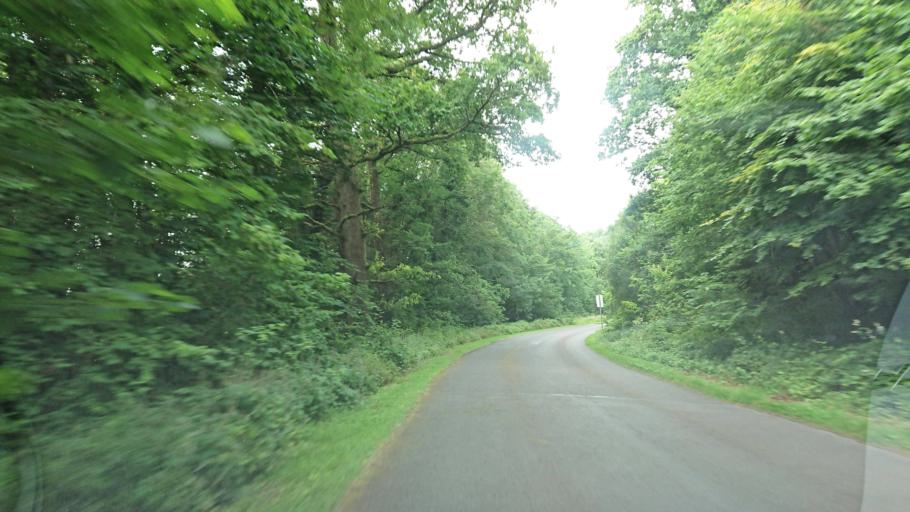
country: IE
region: Connaught
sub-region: Roscommon
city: Boyle
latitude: 53.9754
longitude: -8.2420
